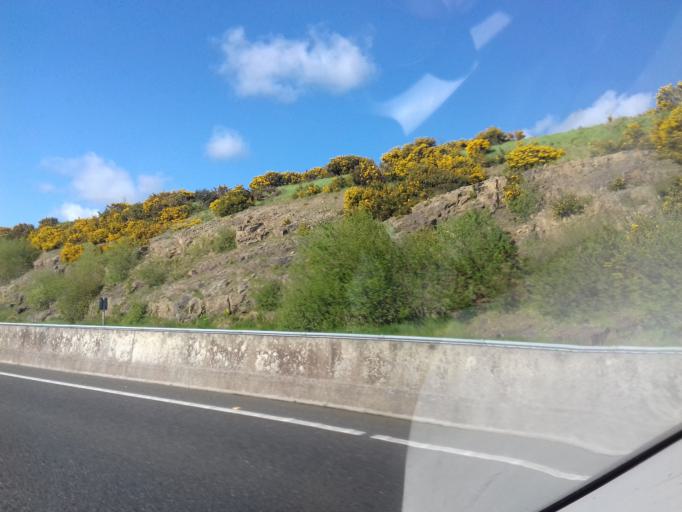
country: IE
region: Leinster
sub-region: Kilkenny
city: Mooncoin
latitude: 52.3430
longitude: -7.1648
